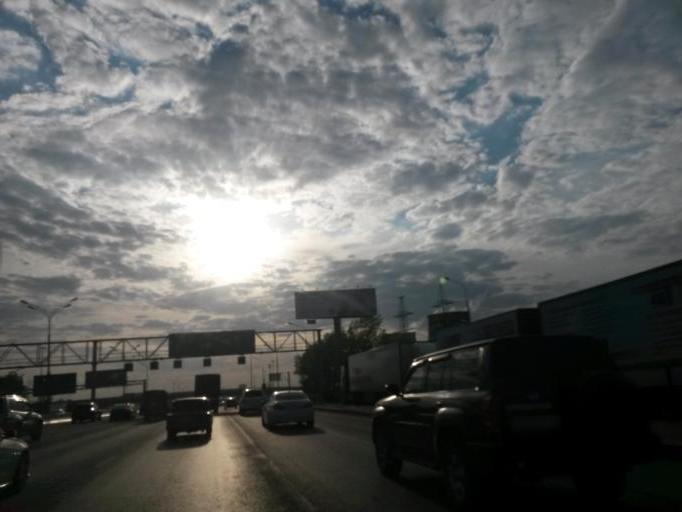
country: RU
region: Moskovskaya
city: Biryulevo Zapadnoye
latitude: 55.5732
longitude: 37.6472
